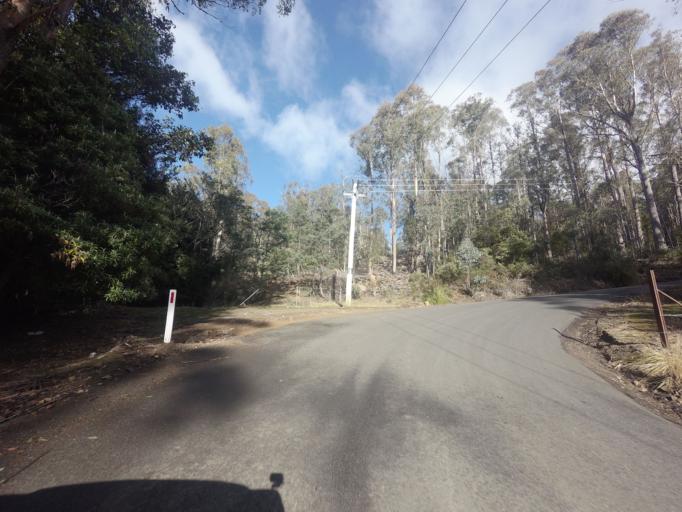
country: AU
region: Tasmania
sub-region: Glenorchy
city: Berriedale
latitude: -42.8415
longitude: 147.1582
